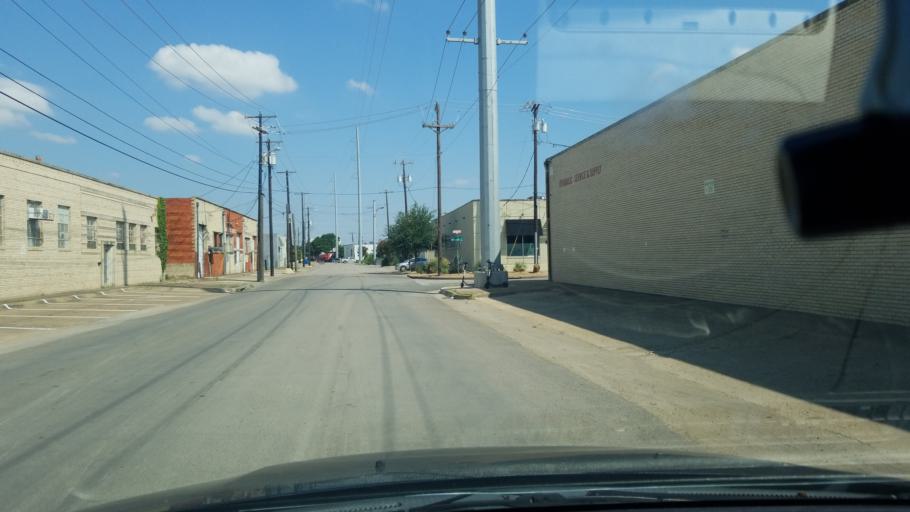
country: US
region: Texas
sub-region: Dallas County
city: Dallas
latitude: 32.7861
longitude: -96.8216
